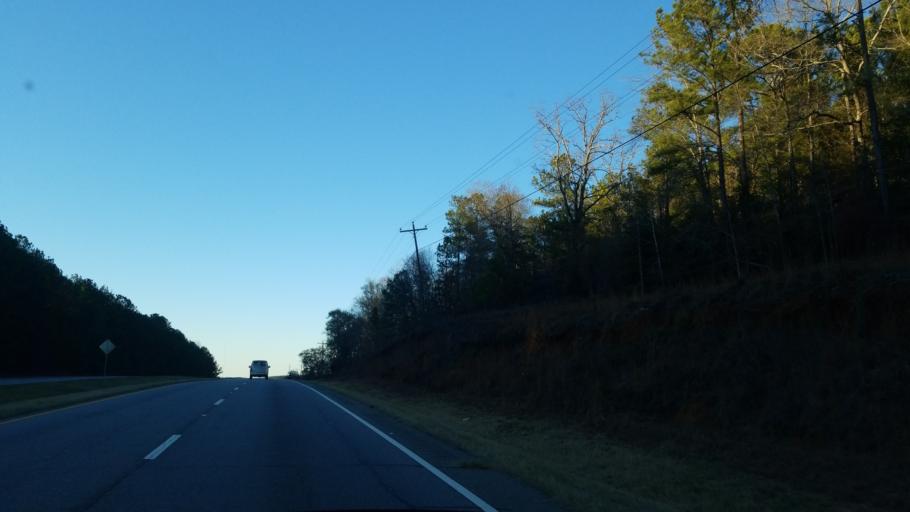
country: US
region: Georgia
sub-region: Chattahoochee County
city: Cusseta
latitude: 32.2546
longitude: -84.7228
